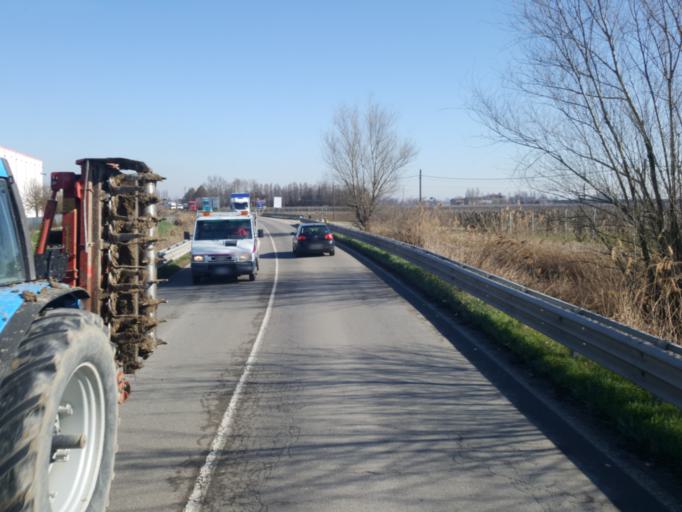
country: IT
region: Emilia-Romagna
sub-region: Provincia di Modena
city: Bomporto
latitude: 44.7375
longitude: 11.0385
